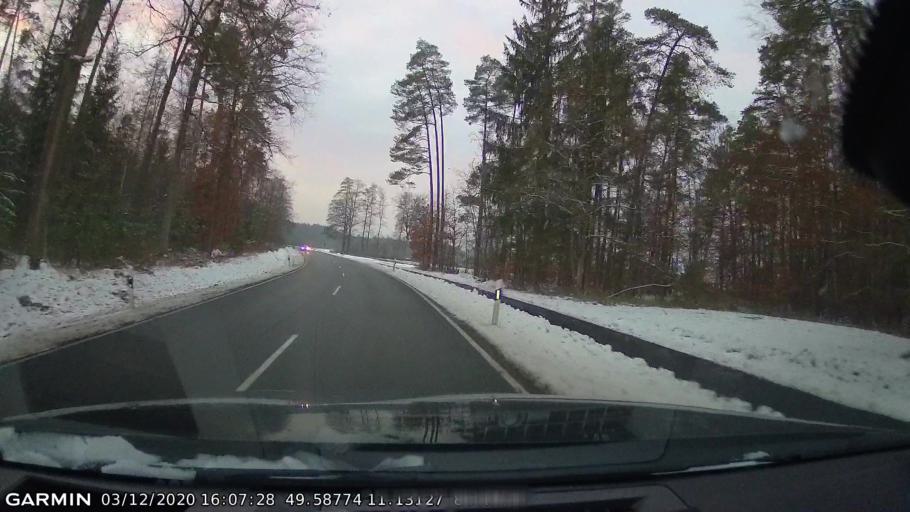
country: DE
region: Bavaria
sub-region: Upper Franconia
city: Dormitz
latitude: 49.5877
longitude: 11.1311
